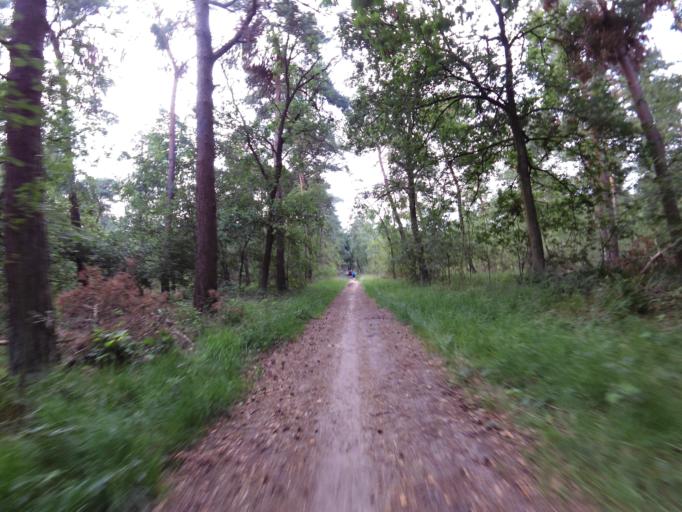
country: NL
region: North Brabant
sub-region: Gemeente Best
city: Best
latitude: 51.5056
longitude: 5.4285
